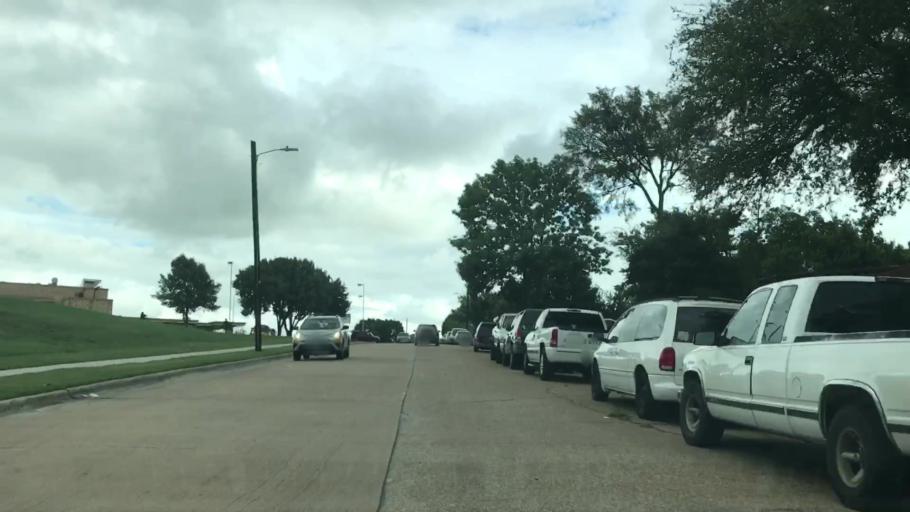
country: US
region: Texas
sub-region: Dallas County
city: Garland
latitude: 32.8973
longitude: -96.6177
